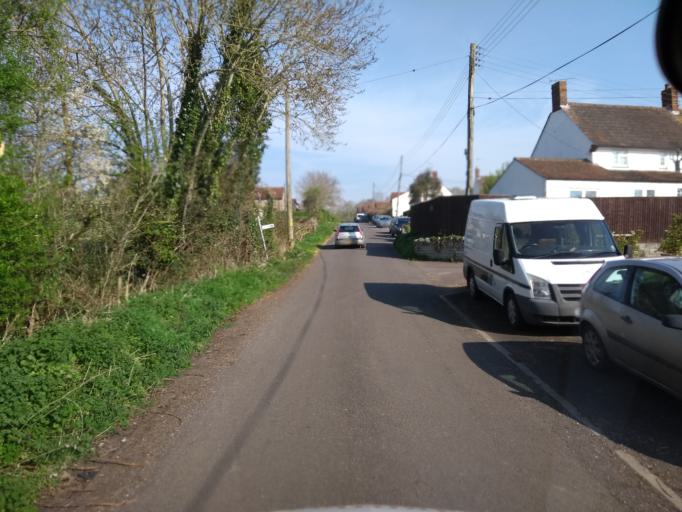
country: GB
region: England
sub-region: Somerset
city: Creech Saint Michael
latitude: 50.9765
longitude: -2.9907
